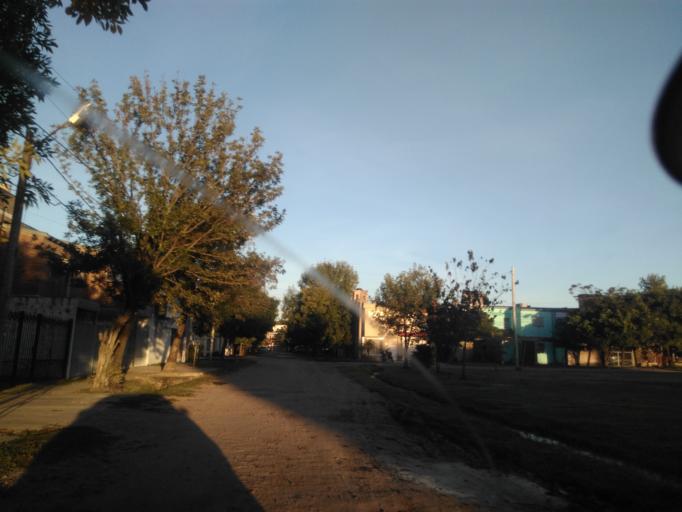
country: AR
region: Chaco
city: Resistencia
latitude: -27.4701
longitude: -58.9831
